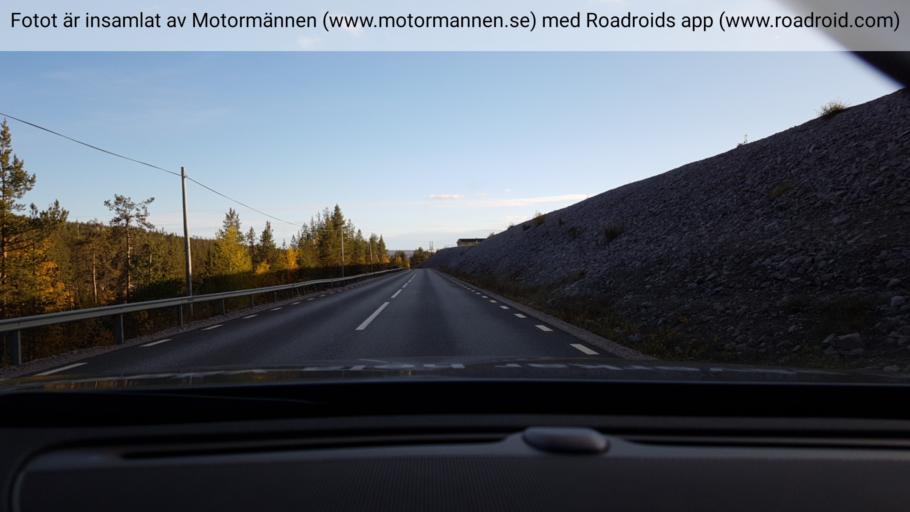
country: SE
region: Norrbotten
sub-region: Jokkmokks Kommun
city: Jokkmokk
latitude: 66.8888
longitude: 19.8290
